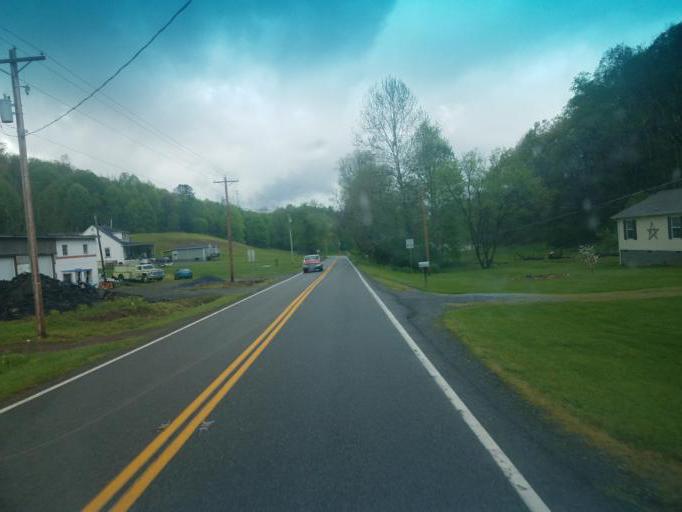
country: US
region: Virginia
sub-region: Washington County
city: Emory
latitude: 36.6463
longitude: -81.7852
